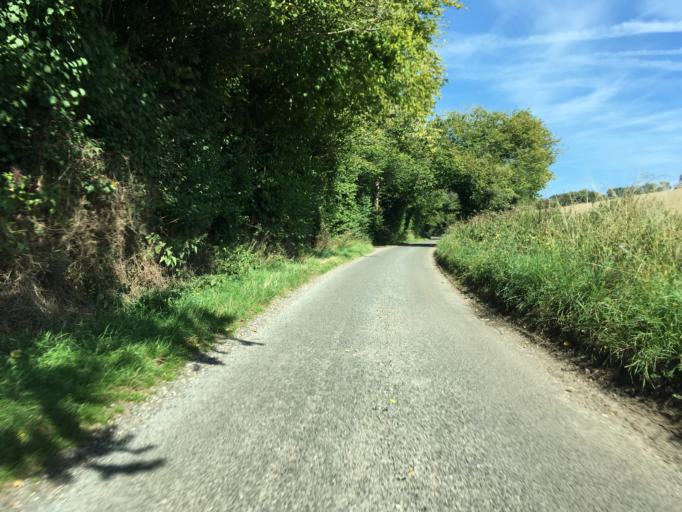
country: GB
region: England
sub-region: Hampshire
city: Highclere
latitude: 51.2820
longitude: -1.3594
